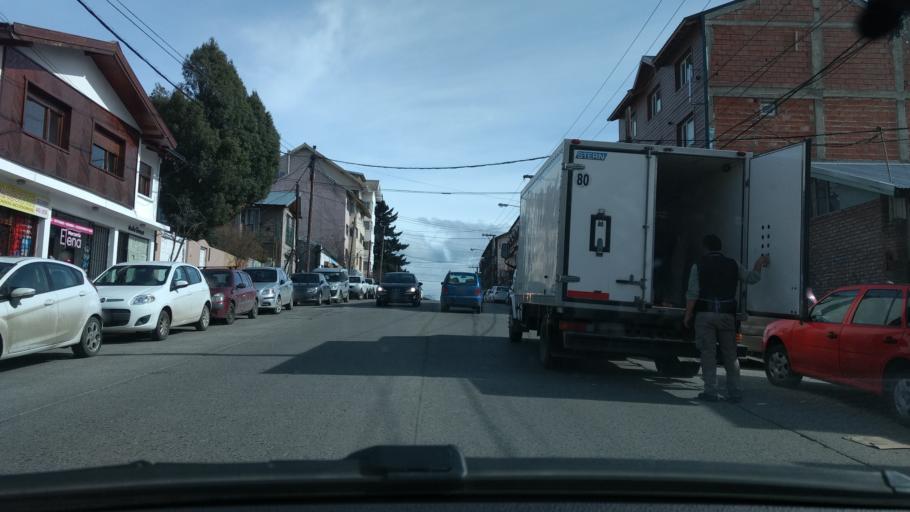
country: AR
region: Rio Negro
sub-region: Departamento de Bariloche
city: San Carlos de Bariloche
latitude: -41.1379
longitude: -71.2991
